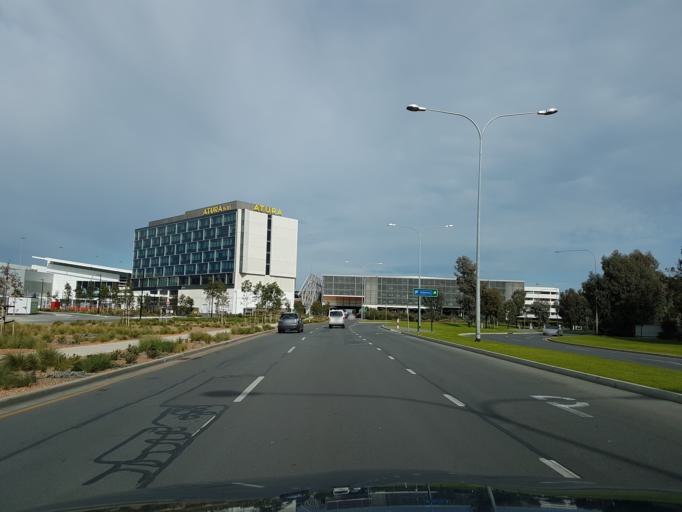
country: AU
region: South Australia
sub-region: City of West Torrens
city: Plympton
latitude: -34.9362
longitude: 138.5389
